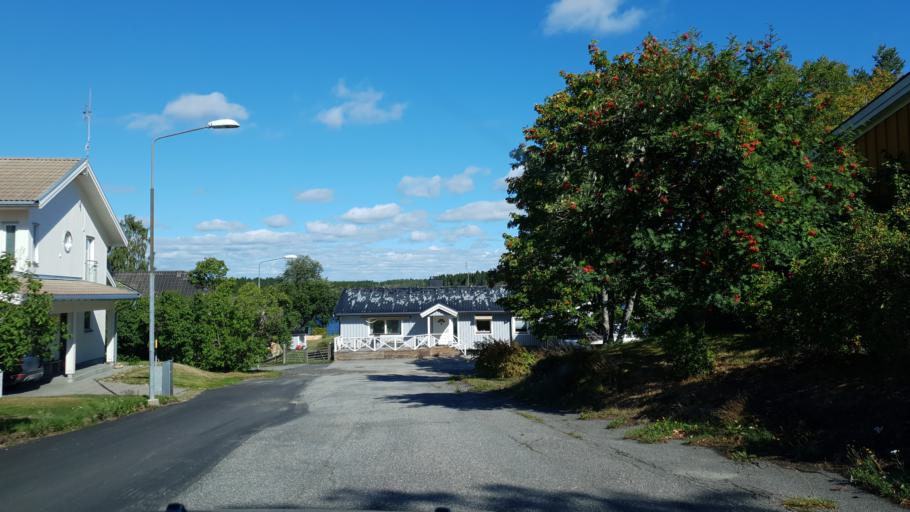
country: SE
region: Vaesterbotten
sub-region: Umea Kommun
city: Holmsund
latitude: 63.7182
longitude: 20.3815
